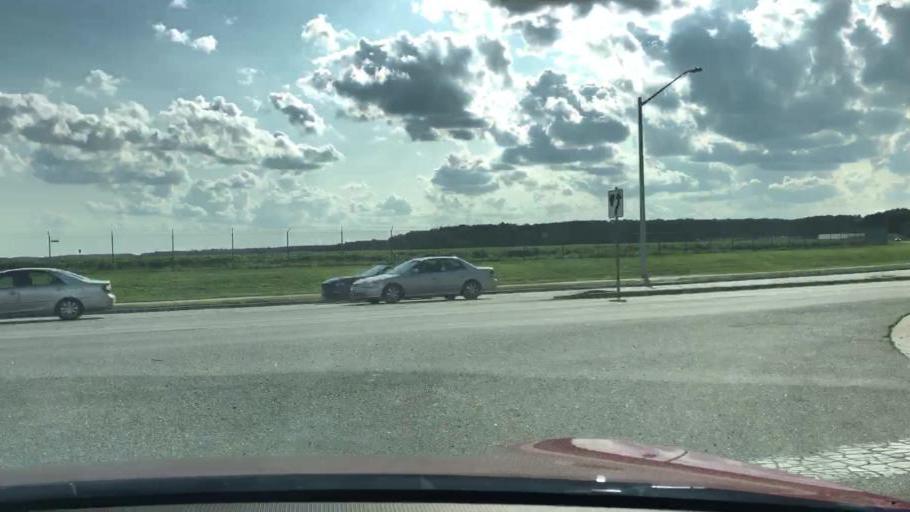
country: US
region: Virginia
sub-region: City of Virginia Beach
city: Virginia Beach
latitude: 36.8378
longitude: -76.0134
